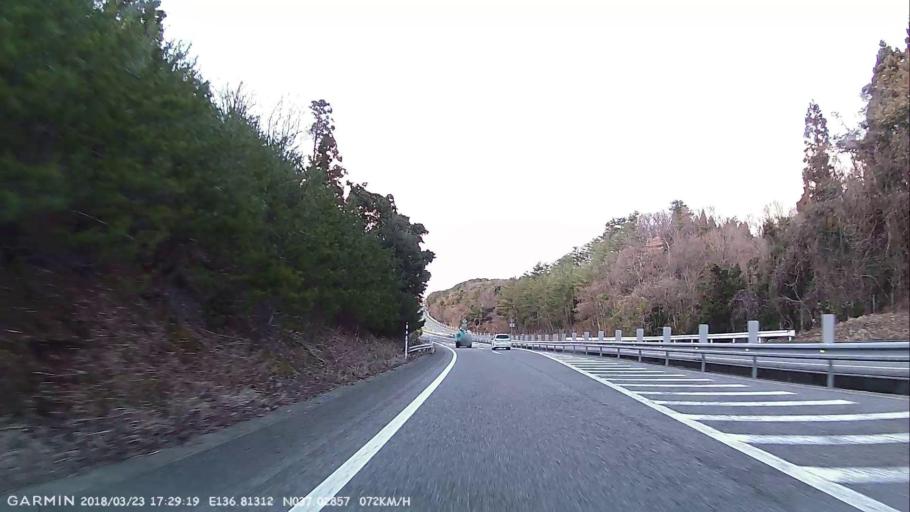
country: JP
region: Ishikawa
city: Hakui
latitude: 37.0287
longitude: 136.8132
